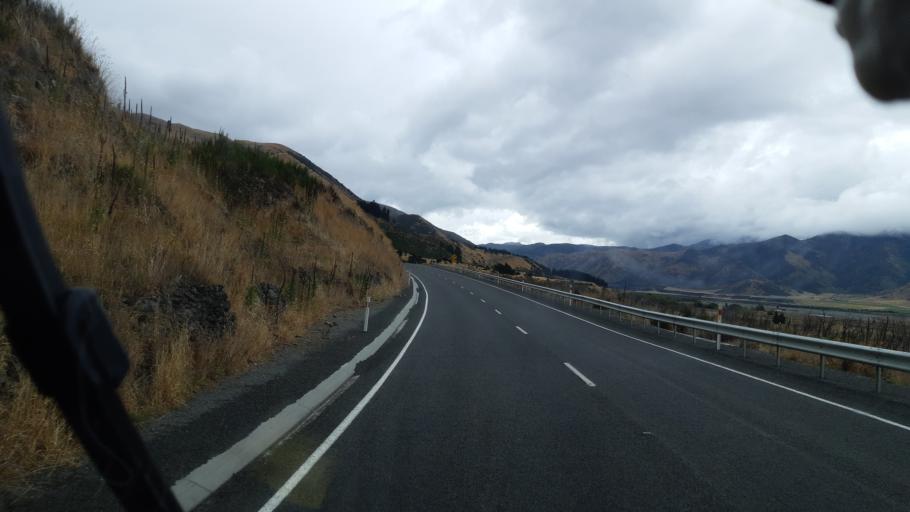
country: NZ
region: Canterbury
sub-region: Hurunui District
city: Amberley
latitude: -42.5765
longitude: 172.7323
